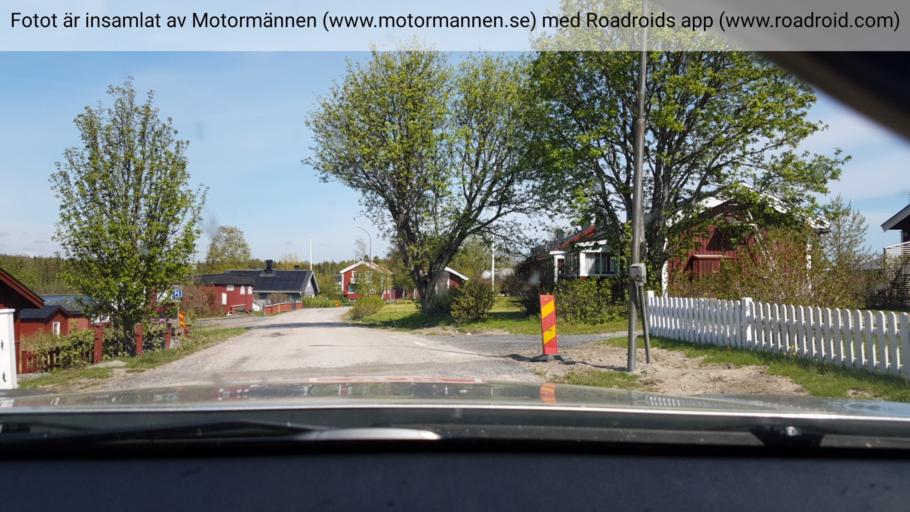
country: SE
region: Vaesterbotten
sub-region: Umea Kommun
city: Taftea
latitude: 63.7984
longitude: 20.5779
